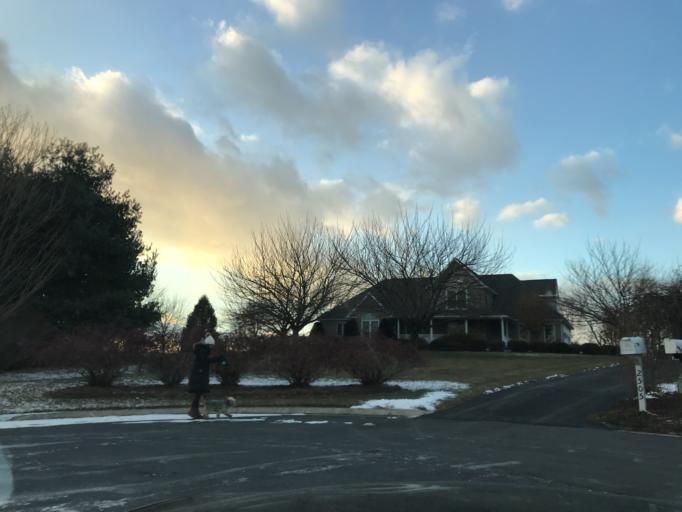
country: US
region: Maryland
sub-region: Harford County
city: Bel Air North
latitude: 39.5912
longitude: -76.3732
